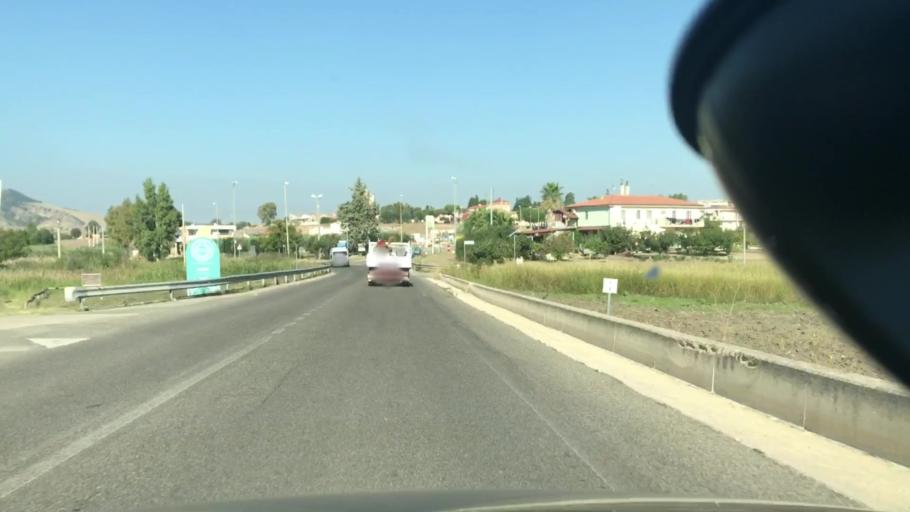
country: IT
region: Basilicate
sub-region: Provincia di Matera
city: La Martella
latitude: 40.6587
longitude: 16.5423
